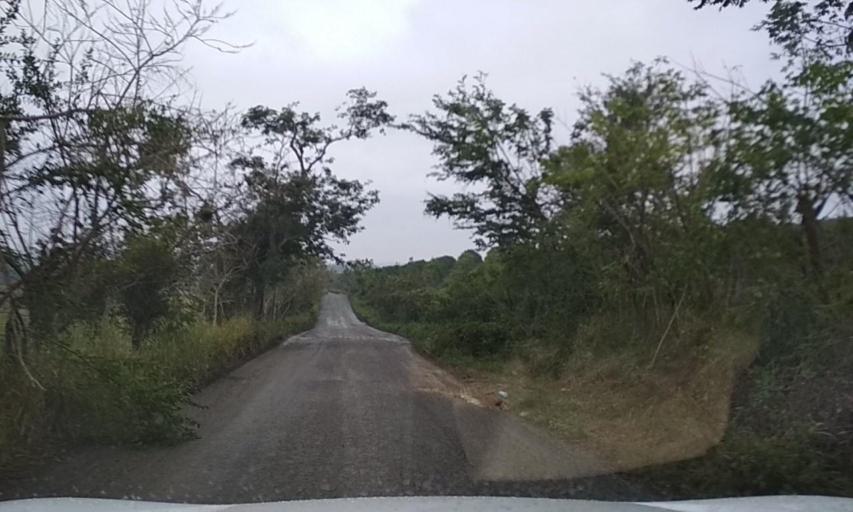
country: MX
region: Veracruz
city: Coatzintla
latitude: 20.4675
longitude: -97.4703
